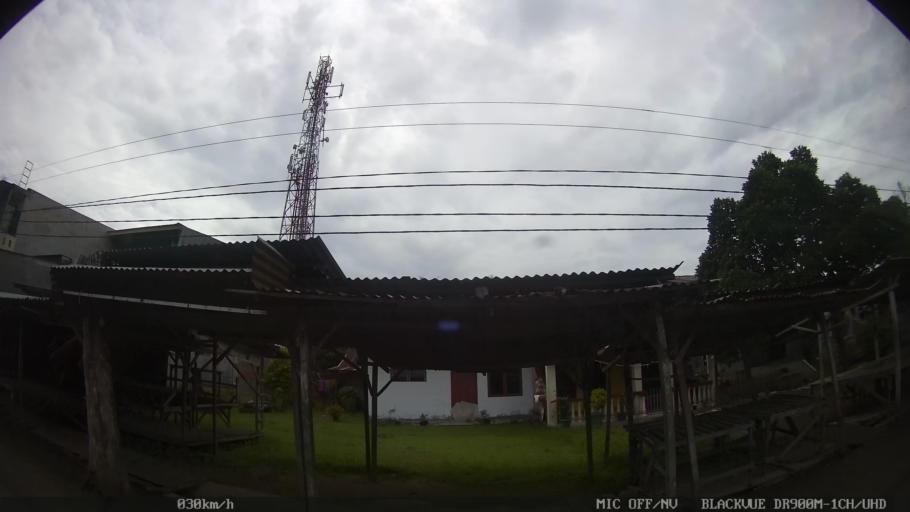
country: ID
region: North Sumatra
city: Sunggal
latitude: 3.5922
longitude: 98.5658
